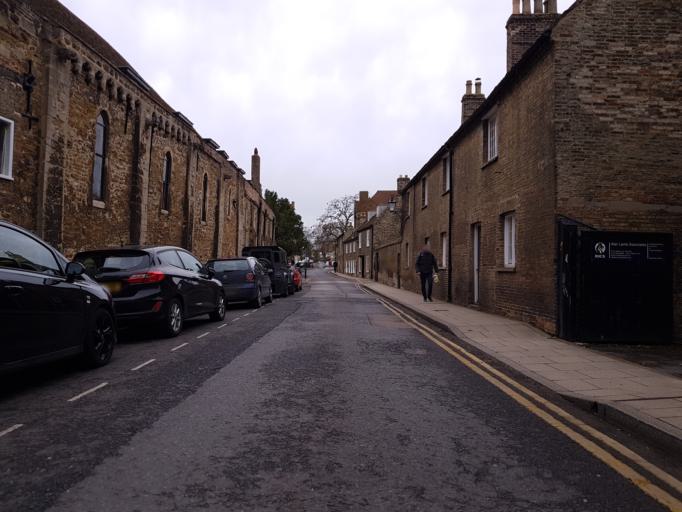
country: GB
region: England
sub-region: Cambridgeshire
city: Ely
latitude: 52.3978
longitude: 0.2622
